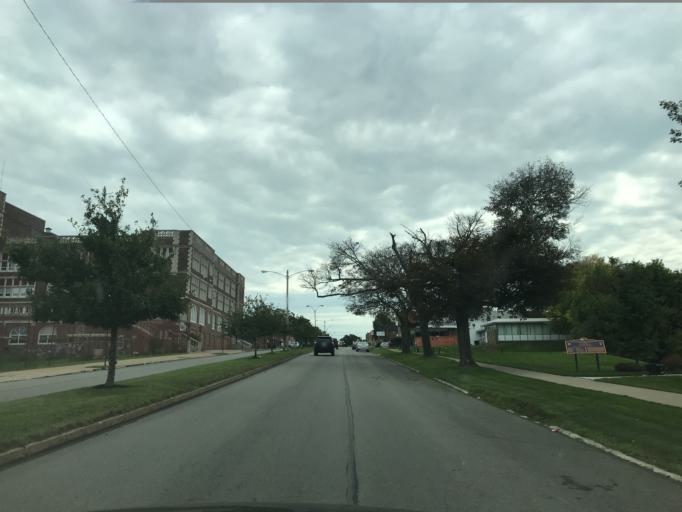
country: US
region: Pennsylvania
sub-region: Erie County
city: Erie
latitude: 42.1109
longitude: -80.0729
